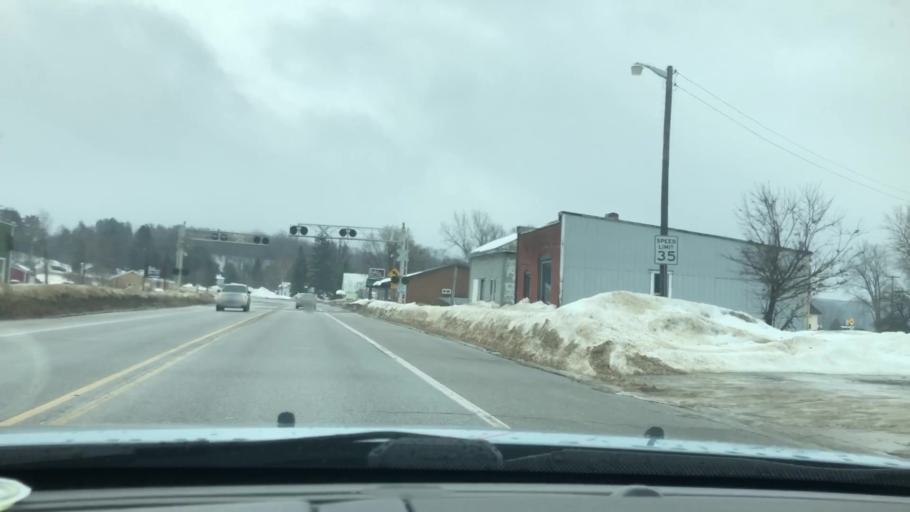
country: US
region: Michigan
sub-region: Otsego County
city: Gaylord
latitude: 45.0640
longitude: -84.8558
